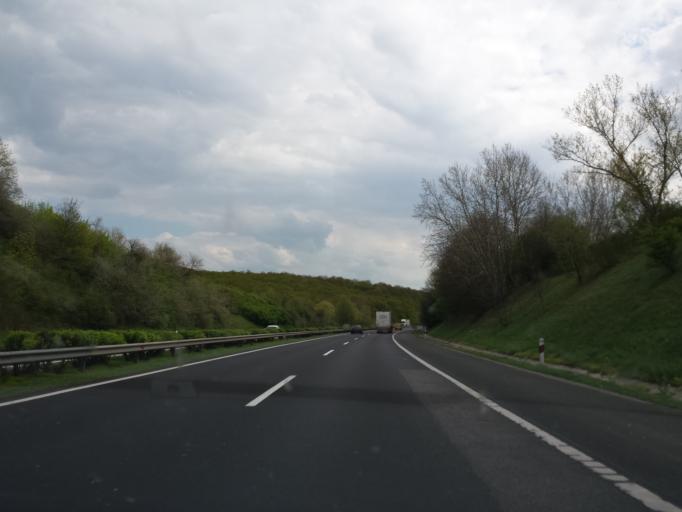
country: HU
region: Komarom-Esztergom
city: Tarjan
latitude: 47.5734
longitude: 18.4712
